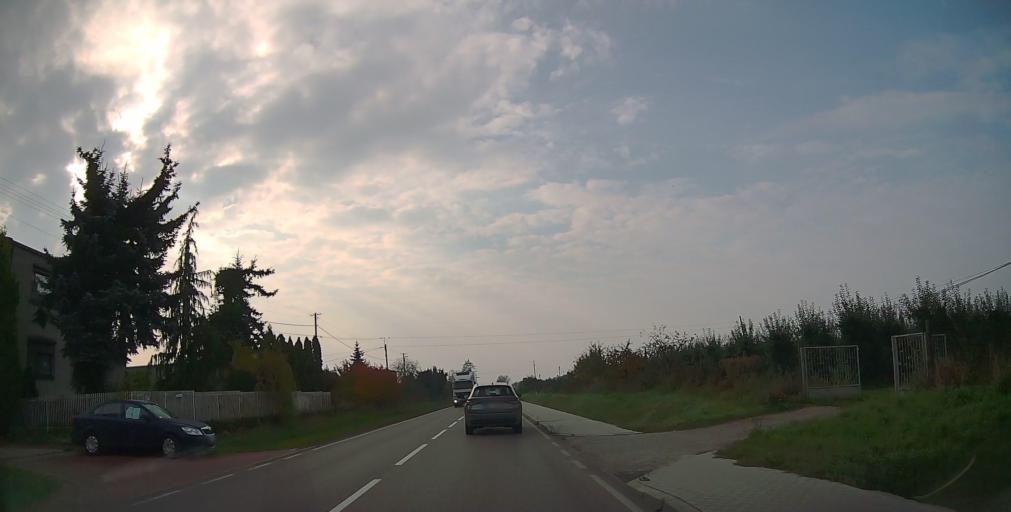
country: PL
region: Masovian Voivodeship
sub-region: Powiat grojecki
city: Belsk Duzy
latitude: 51.7751
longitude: 20.7700
